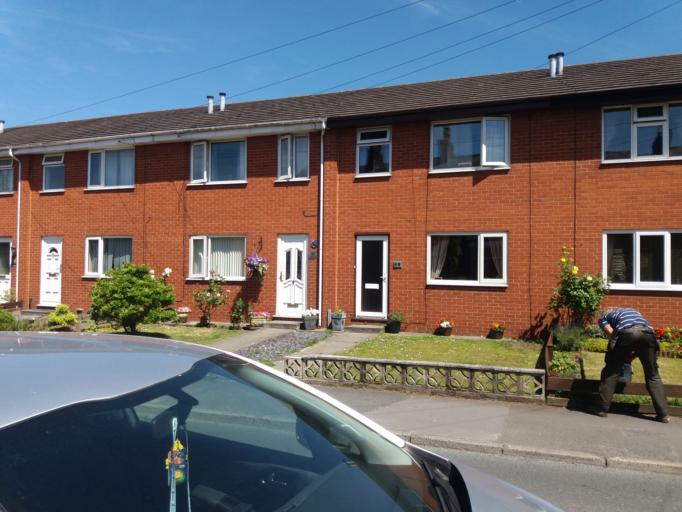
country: GB
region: England
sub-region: Lancashire
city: Croston
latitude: 53.6652
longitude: -2.7759
